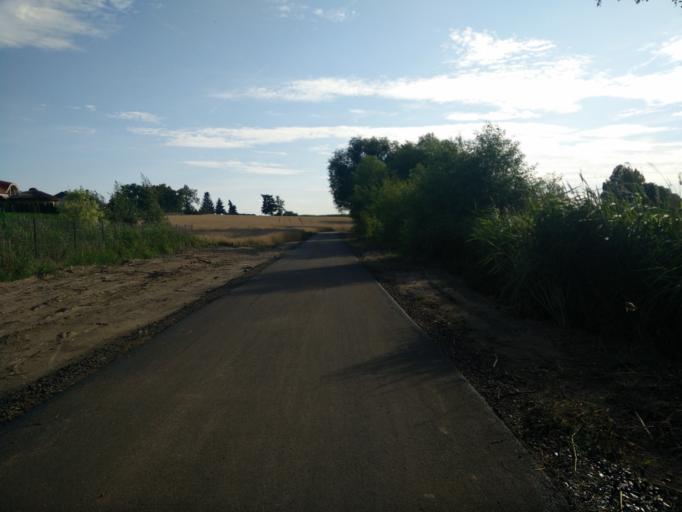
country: PL
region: Greater Poland Voivodeship
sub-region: Powiat sredzki
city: Sroda Wielkopolska
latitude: 52.2517
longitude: 17.3107
